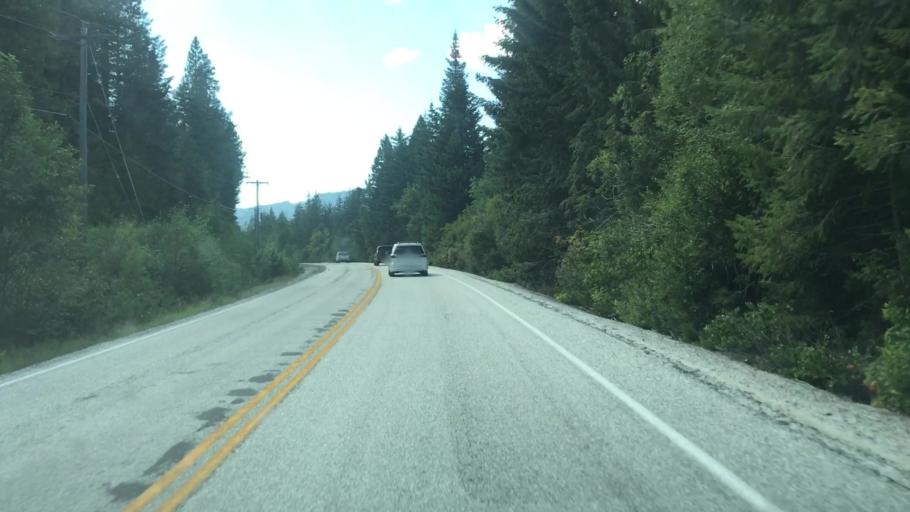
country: US
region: Washington
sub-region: Chelan County
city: Leavenworth
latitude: 47.8277
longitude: -120.7635
